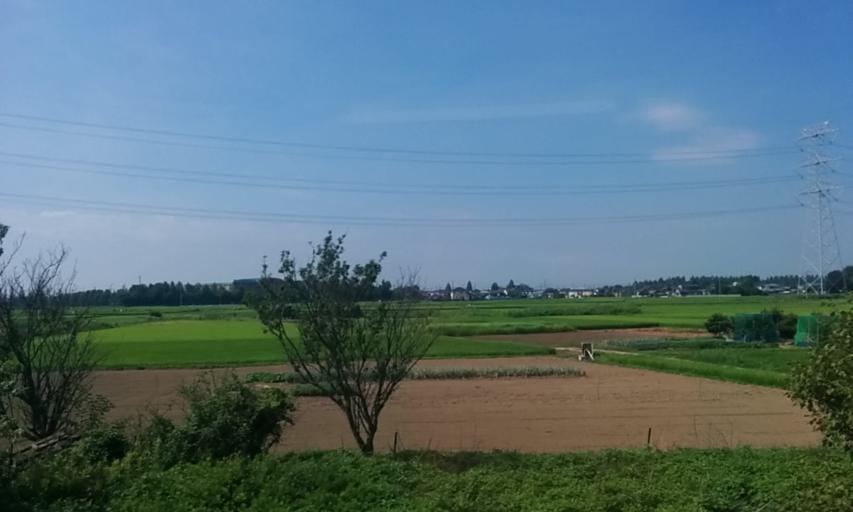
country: JP
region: Saitama
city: Kazo
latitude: 36.1064
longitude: 139.6437
